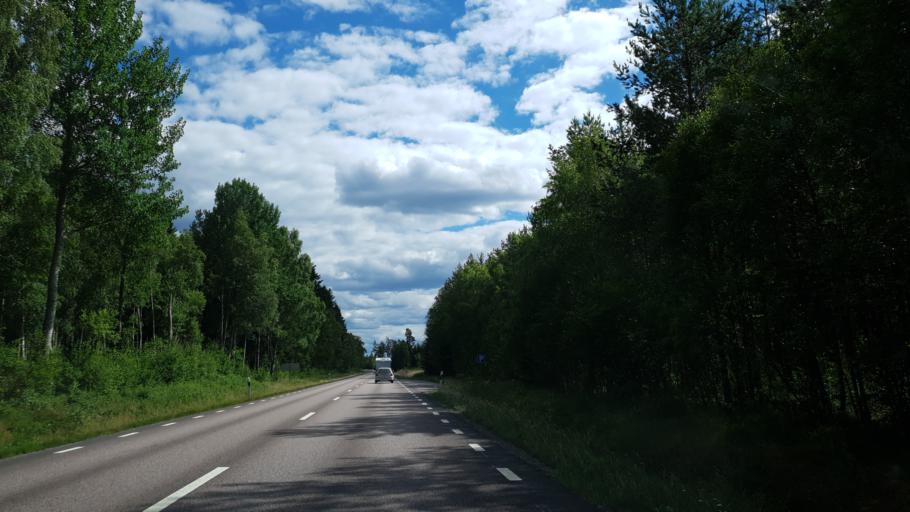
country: SE
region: Kronoberg
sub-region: Lessebo Kommun
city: Lessebo
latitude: 56.8393
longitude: 15.3914
